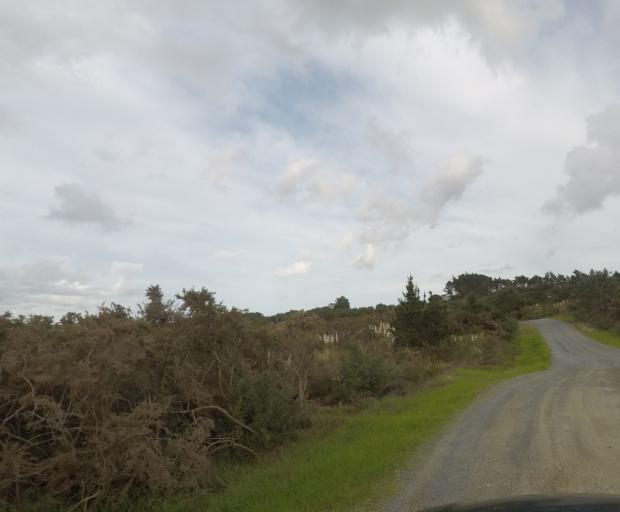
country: NZ
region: Northland
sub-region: Whangarei
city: Ruakaka
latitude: -35.9332
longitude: 174.4585
